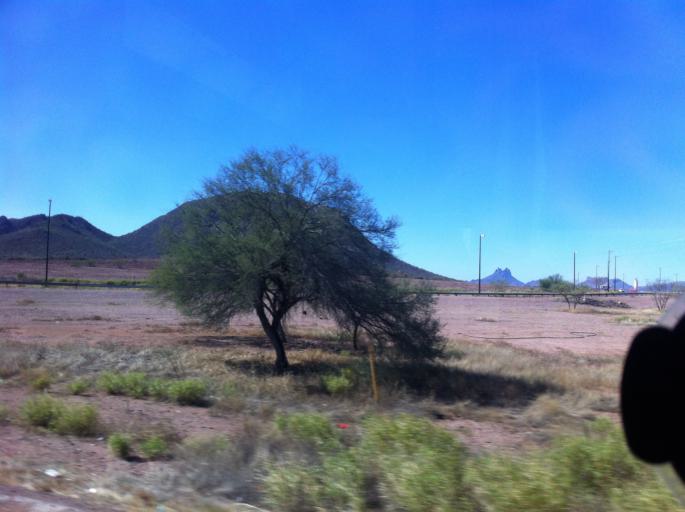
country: MX
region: Sonora
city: Heroica Guaymas
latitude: 27.9888
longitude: -110.9412
